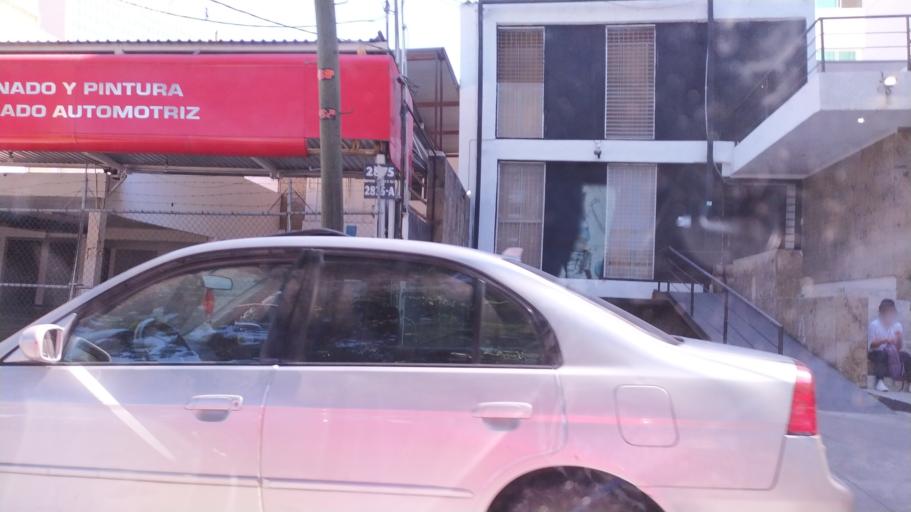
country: MX
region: Jalisco
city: Guadalajara
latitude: 20.6757
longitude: -103.3890
